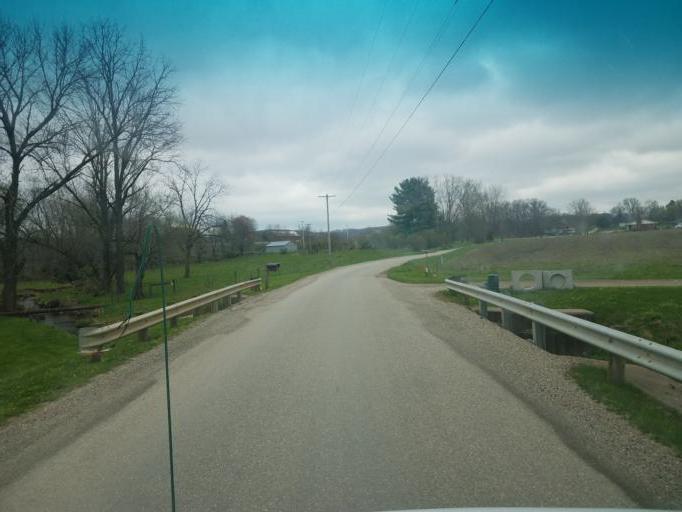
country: US
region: Ohio
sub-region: Stark County
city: Beach City
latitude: 40.6354
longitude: -81.5862
